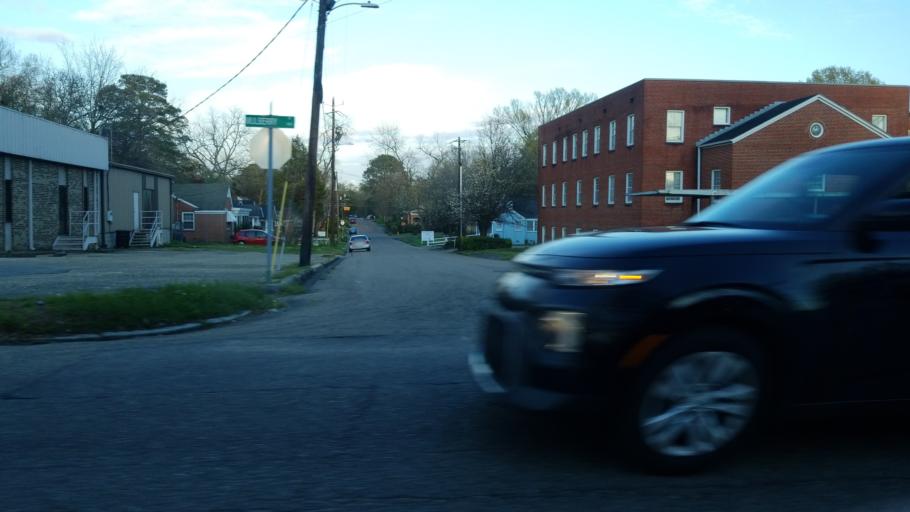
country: US
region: Alabama
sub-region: Montgomery County
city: Montgomery
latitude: 32.3621
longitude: -86.2831
